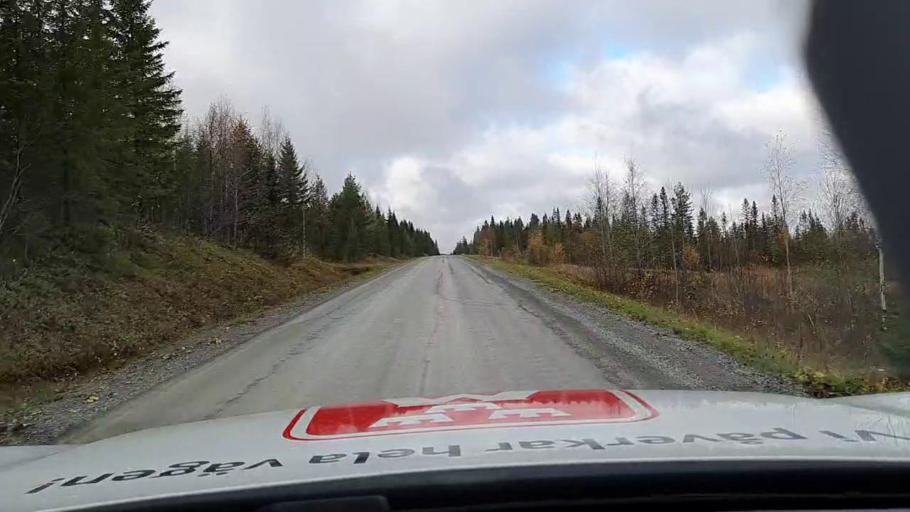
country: SE
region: Jaemtland
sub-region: Bergs Kommun
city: Hoverberg
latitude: 63.0060
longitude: 14.1273
